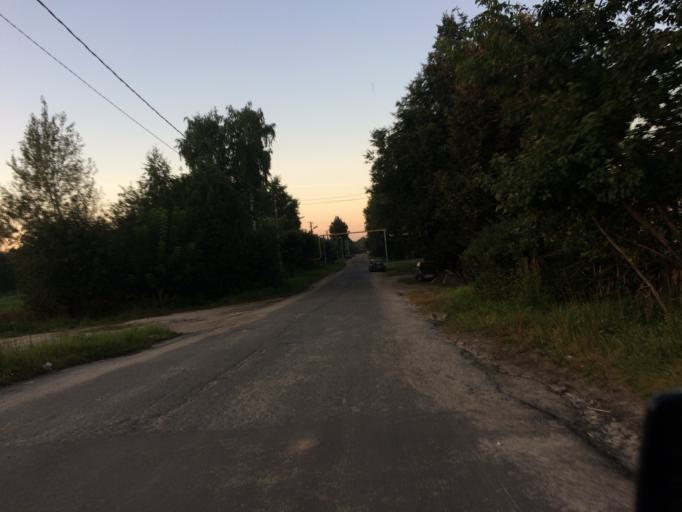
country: RU
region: Mariy-El
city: Yoshkar-Ola
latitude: 56.6384
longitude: 47.9082
